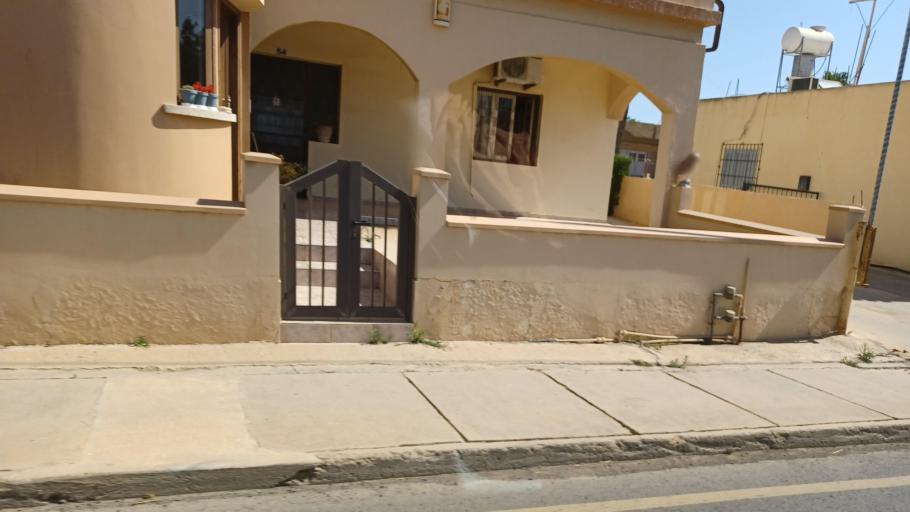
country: CY
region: Ammochostos
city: Frenaros
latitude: 35.0282
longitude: 33.9466
